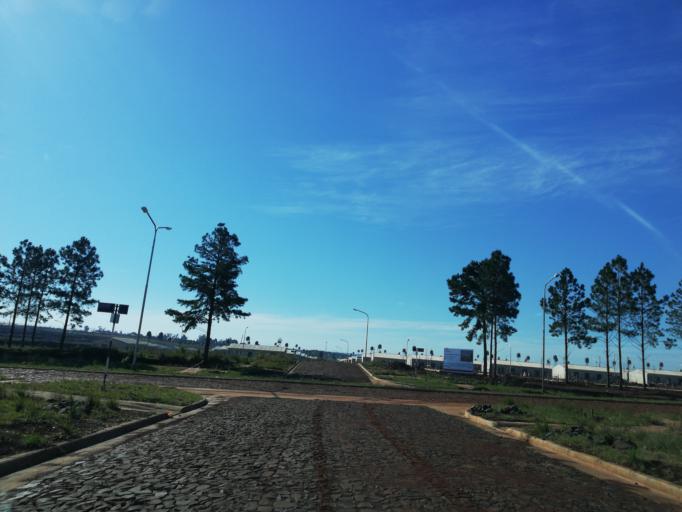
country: AR
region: Misiones
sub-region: Departamento de Capital
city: Posadas
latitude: -27.4063
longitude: -55.9957
